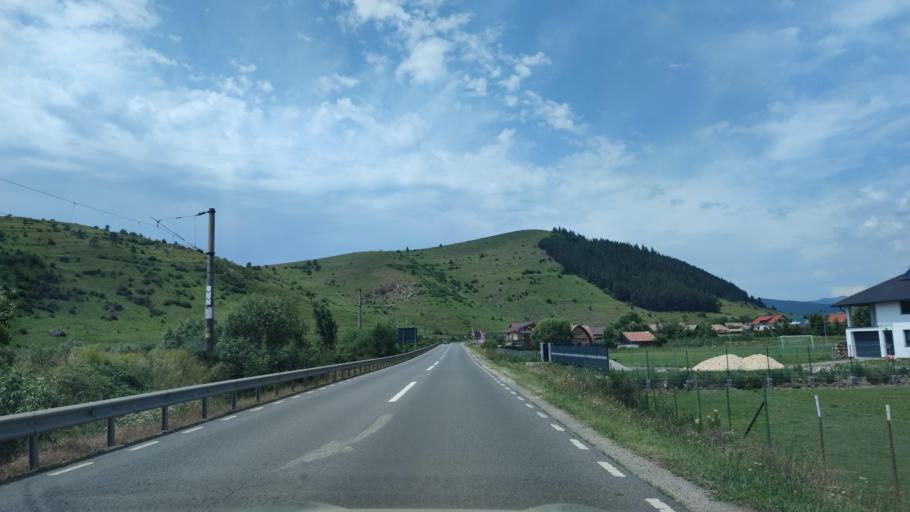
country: RO
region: Harghita
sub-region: Comuna Sandominic
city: Sandominic
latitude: 46.5746
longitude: 25.7921
